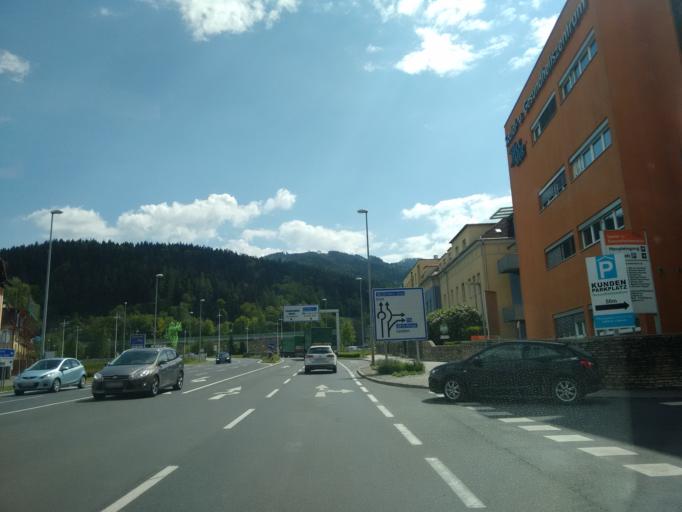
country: AT
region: Styria
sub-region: Politischer Bezirk Bruck-Muerzzuschlag
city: Bruck an der Mur
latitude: 47.4082
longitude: 15.2741
